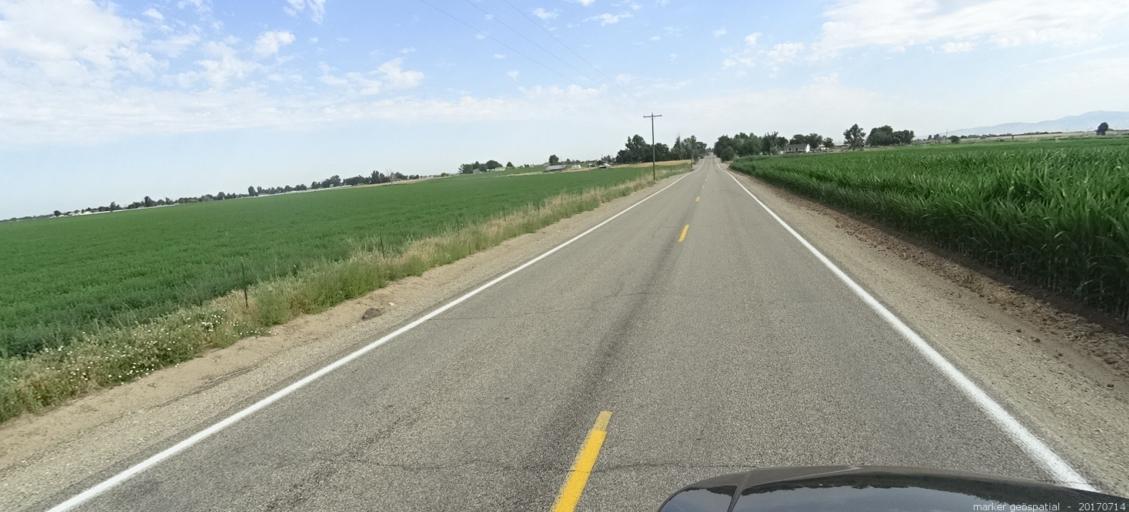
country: US
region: Idaho
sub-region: Ada County
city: Kuna
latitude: 43.4678
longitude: -116.3545
